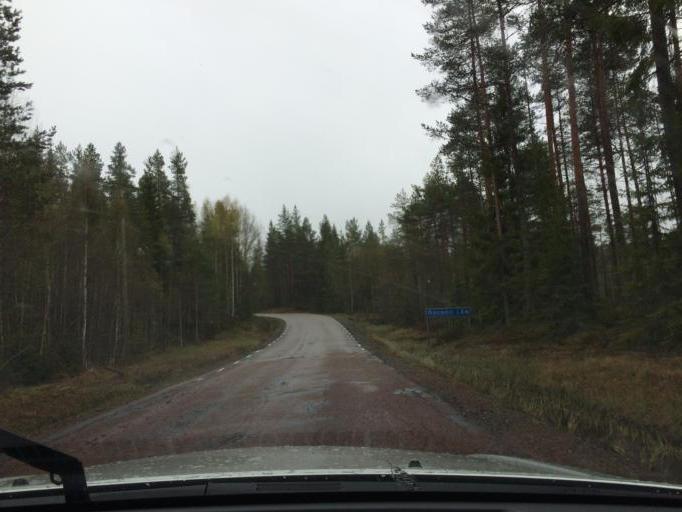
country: SE
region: Dalarna
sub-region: Ludvika Kommun
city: Abborrberget
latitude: 60.0446
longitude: 14.7442
